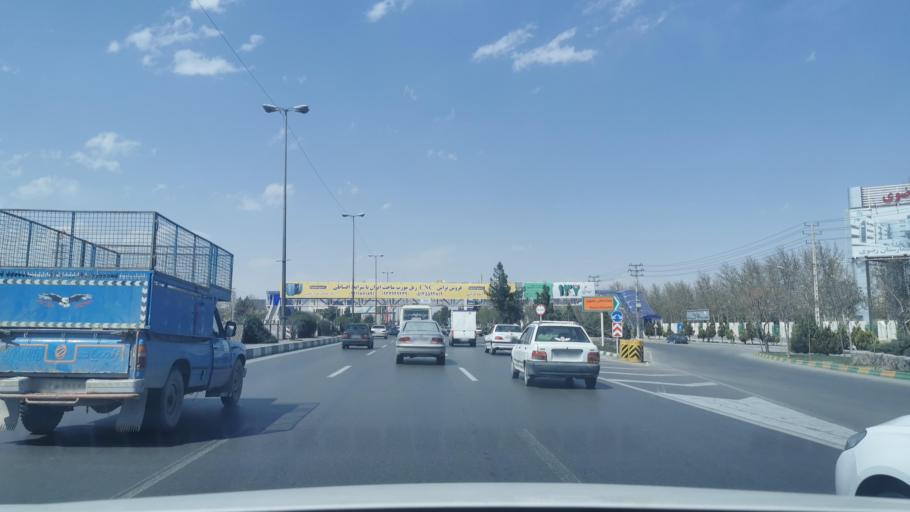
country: IR
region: Razavi Khorasan
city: Mashhad
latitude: 36.3528
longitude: 59.5442
